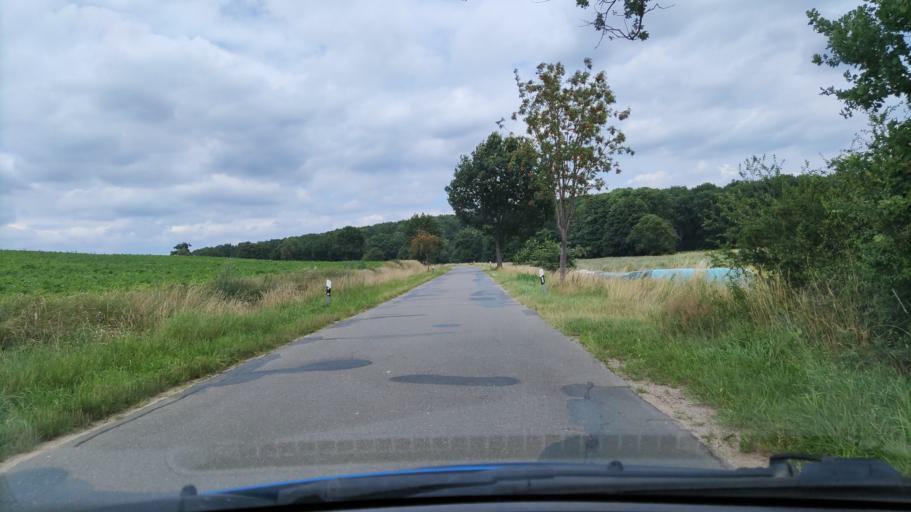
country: DE
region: Lower Saxony
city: Weste
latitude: 53.0771
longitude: 10.6894
